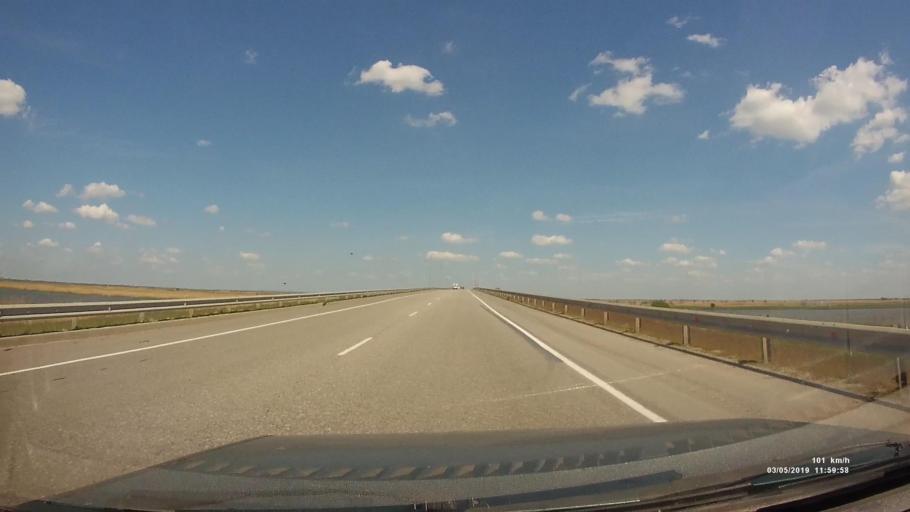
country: RU
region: Rostov
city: Bagayevskaya
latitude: 47.2425
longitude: 40.3356
